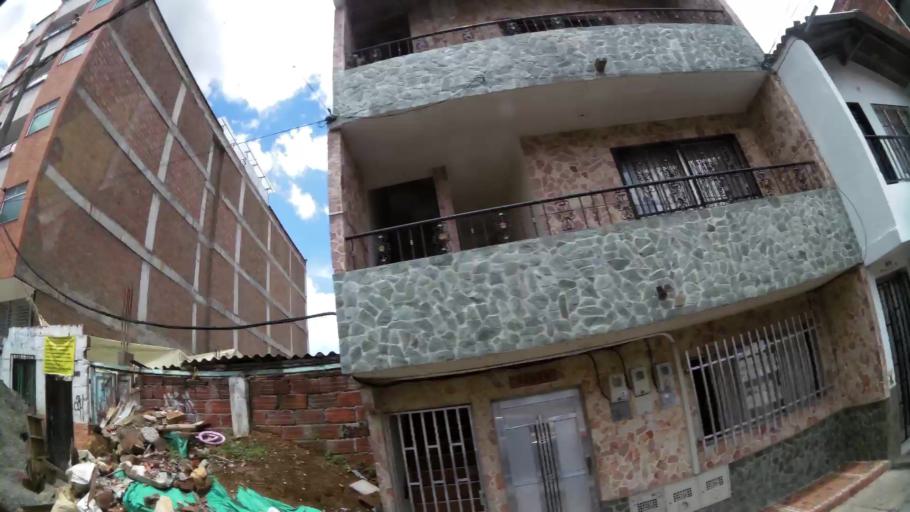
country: CO
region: Antioquia
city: La Estrella
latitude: 6.1567
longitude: -75.6399
